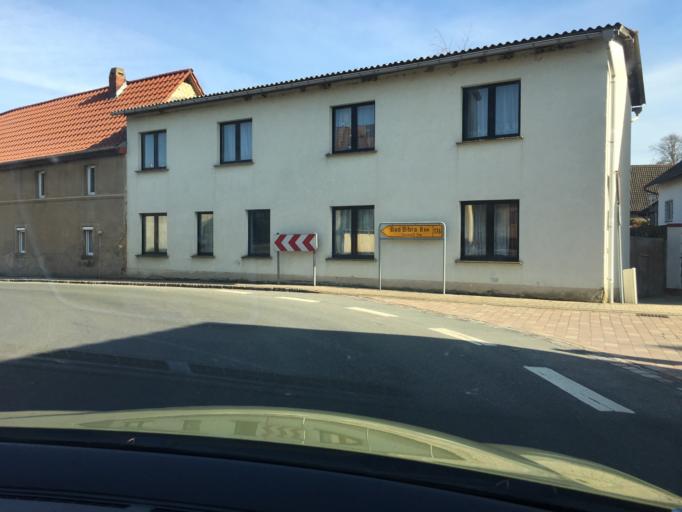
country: DE
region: Thuringia
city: Rastenberg
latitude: 51.2149
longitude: 11.4808
